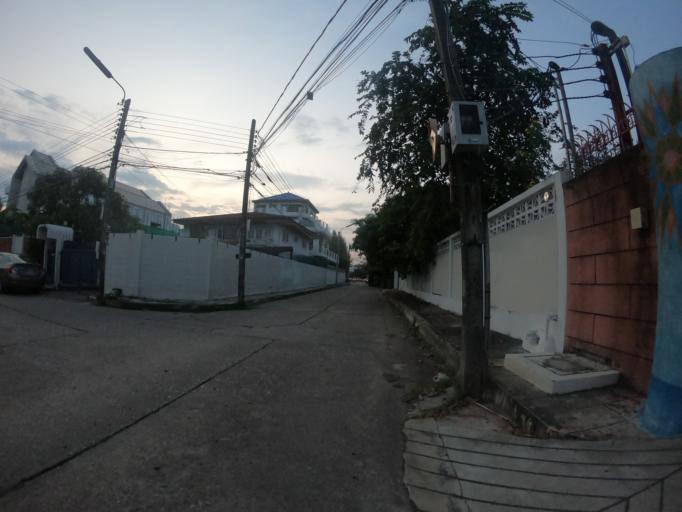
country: TH
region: Bangkok
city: Lat Phrao
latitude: 13.8289
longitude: 100.6109
